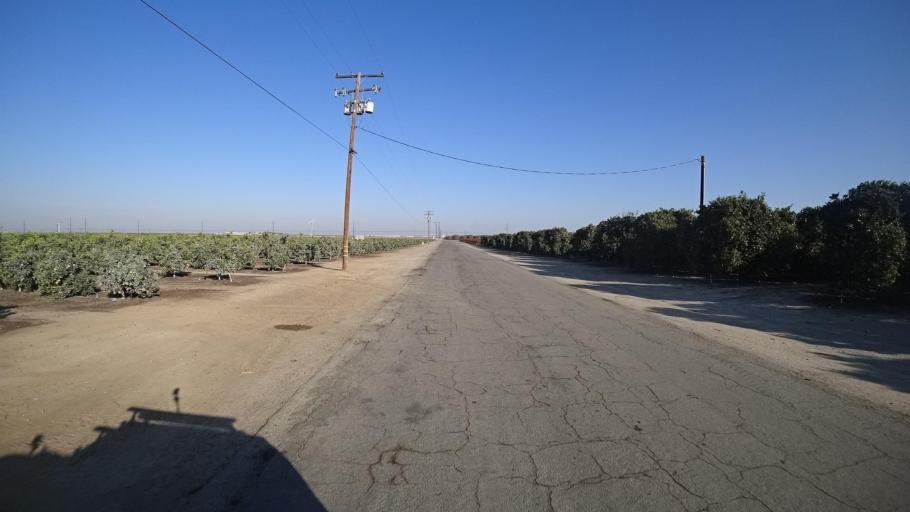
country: US
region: California
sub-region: Tulare County
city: Richgrove
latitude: 35.7730
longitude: -119.1518
